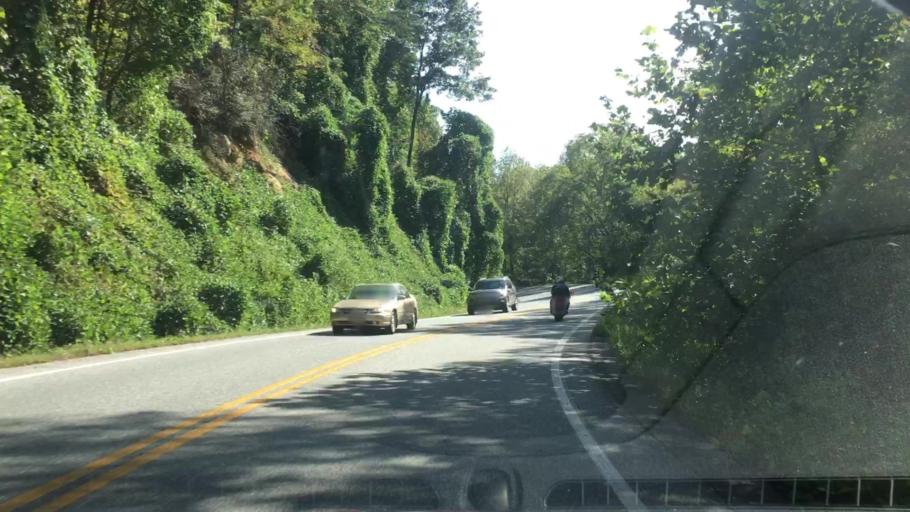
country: US
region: Georgia
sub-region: White County
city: Cleveland
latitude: 34.6673
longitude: -83.9024
